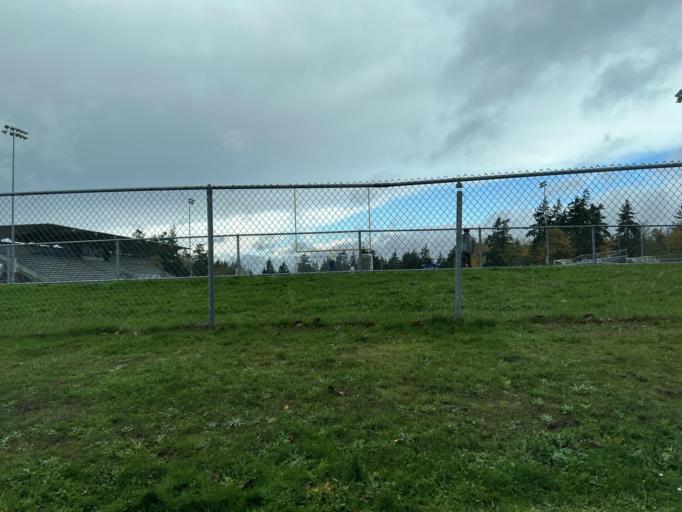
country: US
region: Washington
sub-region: Kitsap County
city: Bainbridge Island
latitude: 47.6378
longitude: -122.5235
